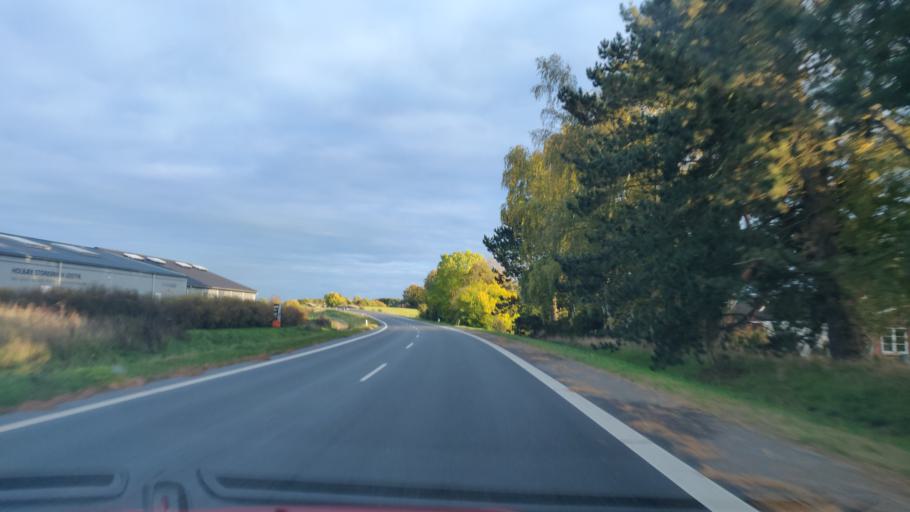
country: DK
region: Zealand
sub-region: Holbaek Kommune
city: Holbaek
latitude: 55.6862
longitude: 11.7011
